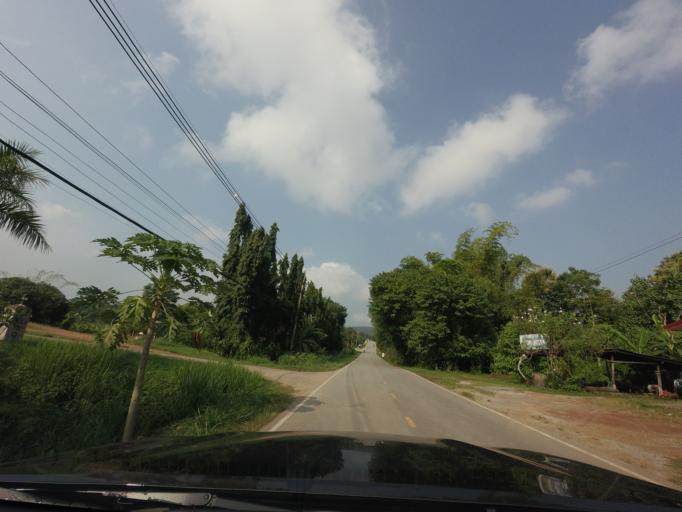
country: TH
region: Loei
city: Chiang Khan
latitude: 17.8909
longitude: 101.6444
